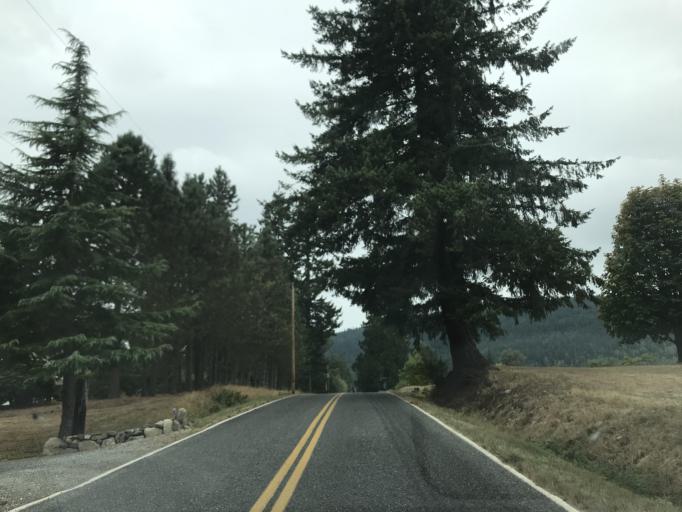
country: US
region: Washington
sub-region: Whatcom County
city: Sudden Valley
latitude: 48.7749
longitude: -122.3351
